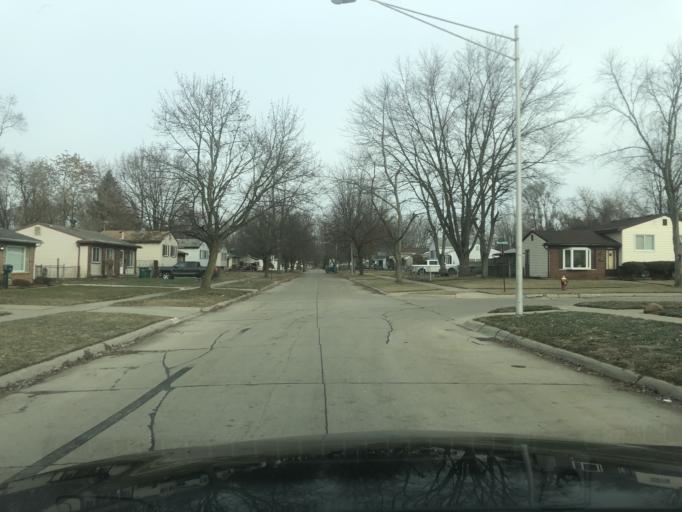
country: US
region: Michigan
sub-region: Wayne County
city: Taylor
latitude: 42.1893
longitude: -83.3193
